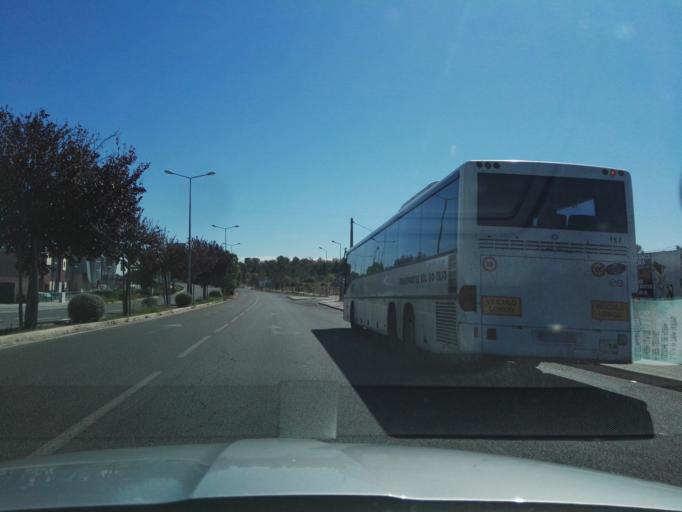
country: PT
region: Setubal
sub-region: Alcochete
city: Alcochete
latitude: 38.7513
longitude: -8.9430
